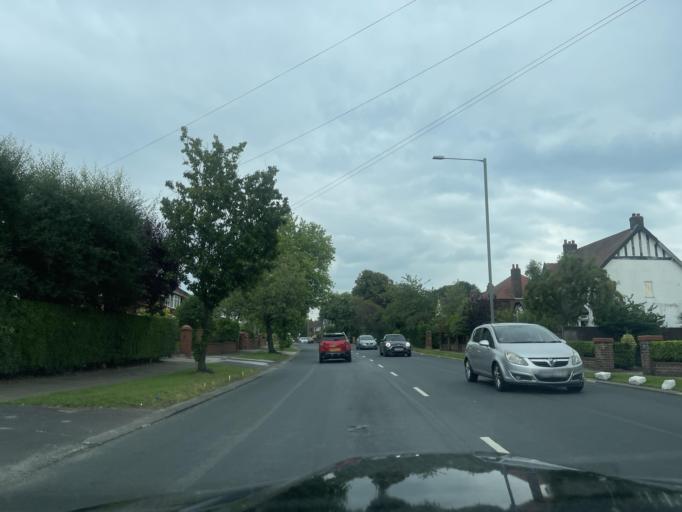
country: GB
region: England
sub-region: Lancashire
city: Leyland
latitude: 53.6878
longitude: -2.7087
